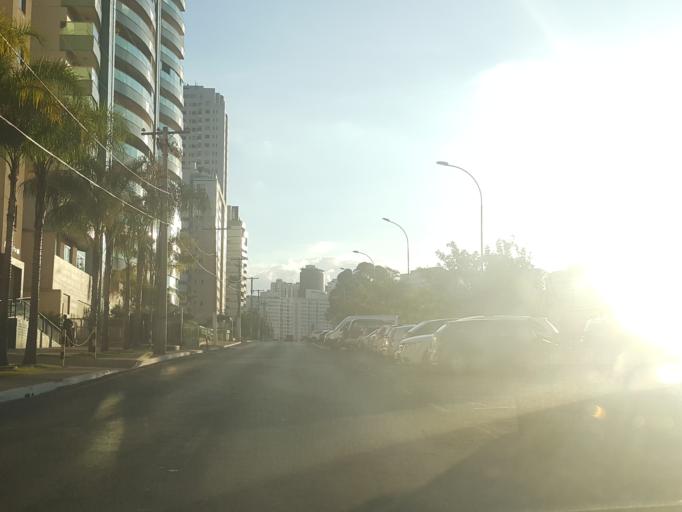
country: BR
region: Federal District
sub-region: Brasilia
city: Brasilia
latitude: -15.8347
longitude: -48.0280
